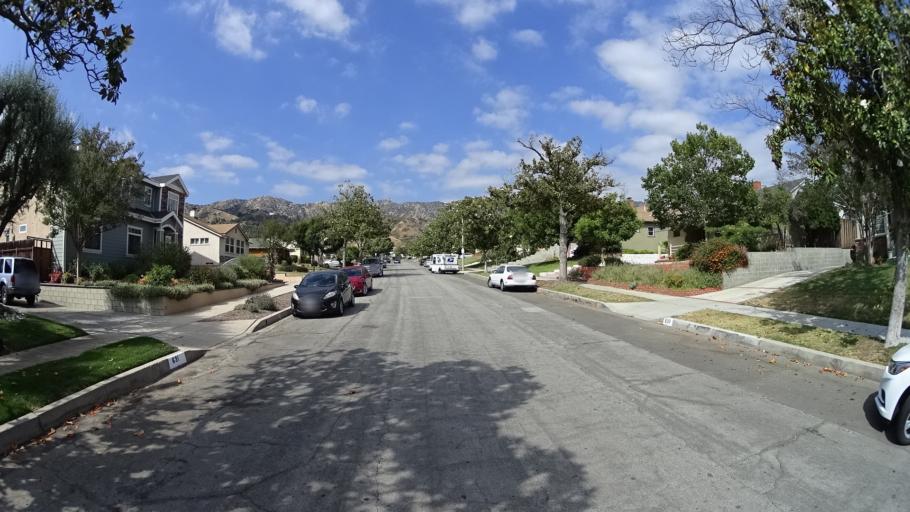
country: US
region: California
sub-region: Los Angeles County
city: Burbank
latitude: 34.1953
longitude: -118.3152
